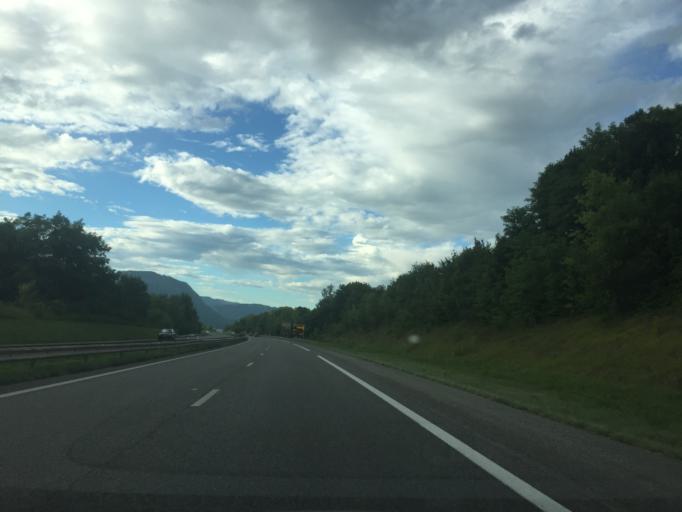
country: FR
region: Rhone-Alpes
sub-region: Departement de la Savoie
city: Mouxy
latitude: 45.6880
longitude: 5.9326
